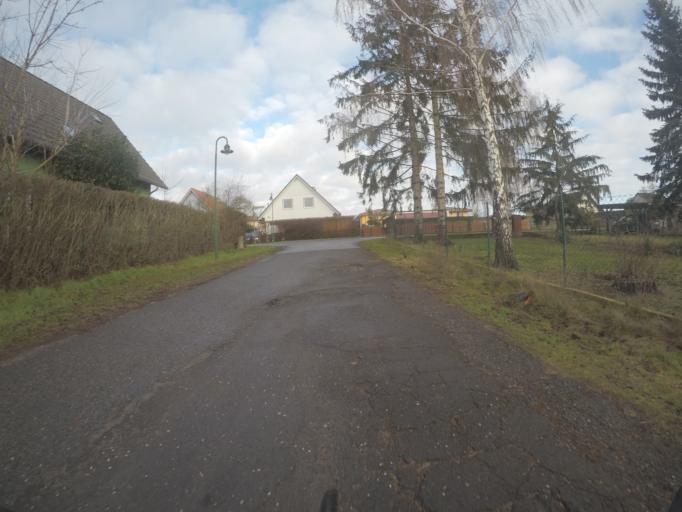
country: DE
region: Berlin
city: Falkenberg
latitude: 52.5902
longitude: 13.5386
